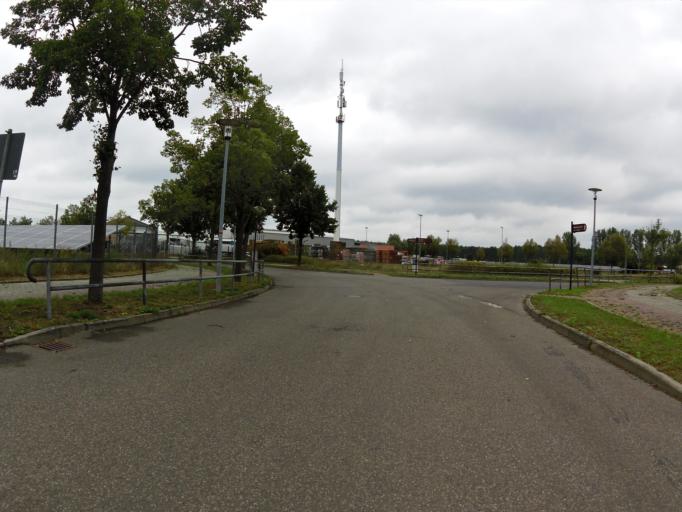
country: DE
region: Brandenburg
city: Storkow
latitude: 52.2670
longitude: 13.9442
